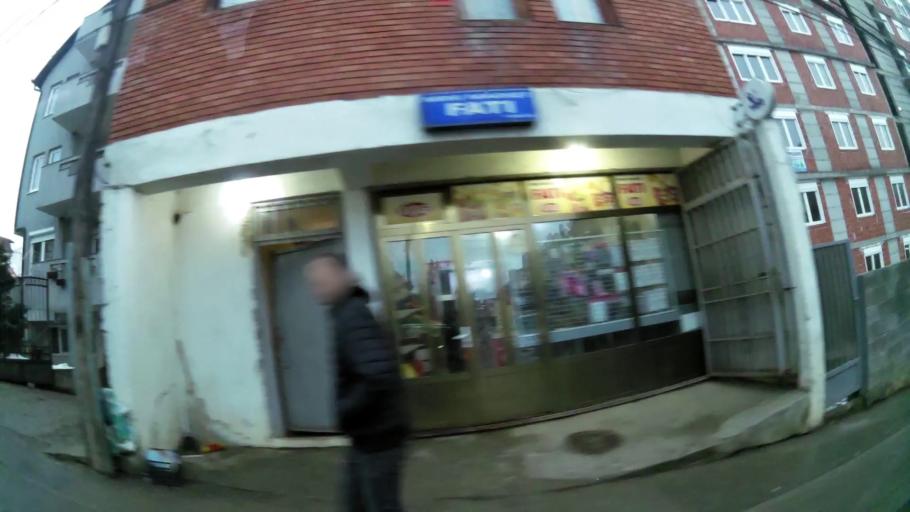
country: XK
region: Pristina
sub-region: Komuna e Prishtines
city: Pristina
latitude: 42.6574
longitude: 21.1731
